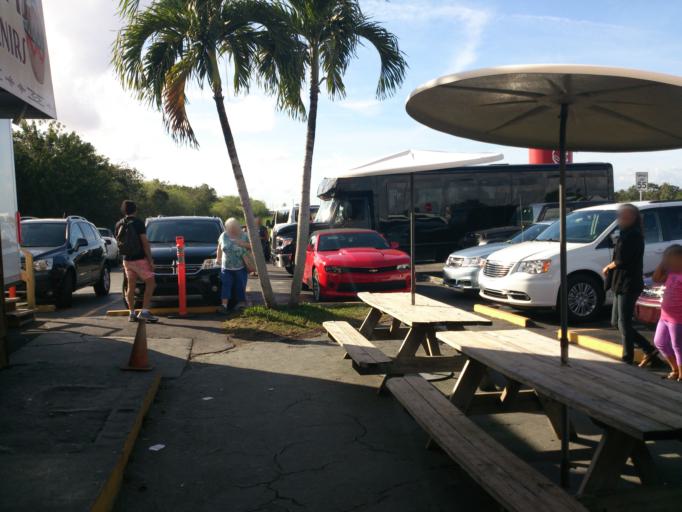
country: US
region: Florida
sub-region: Miami-Dade County
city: Kendall West
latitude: 25.7607
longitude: -80.5811
